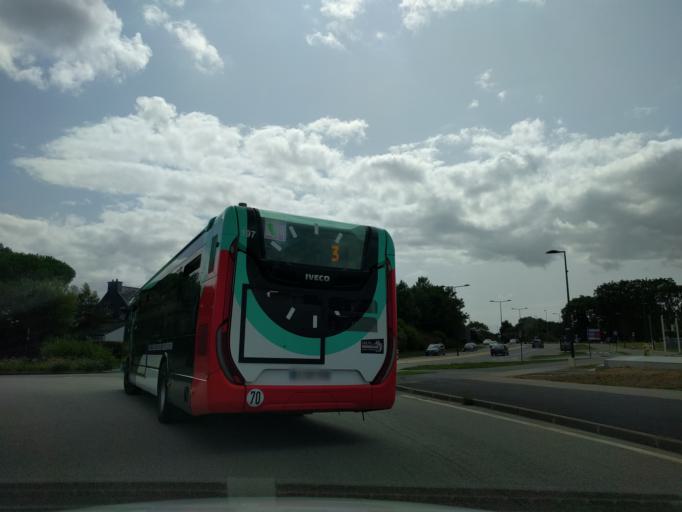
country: FR
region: Brittany
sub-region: Departement du Morbihan
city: Vannes
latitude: 47.6504
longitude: -2.7232
